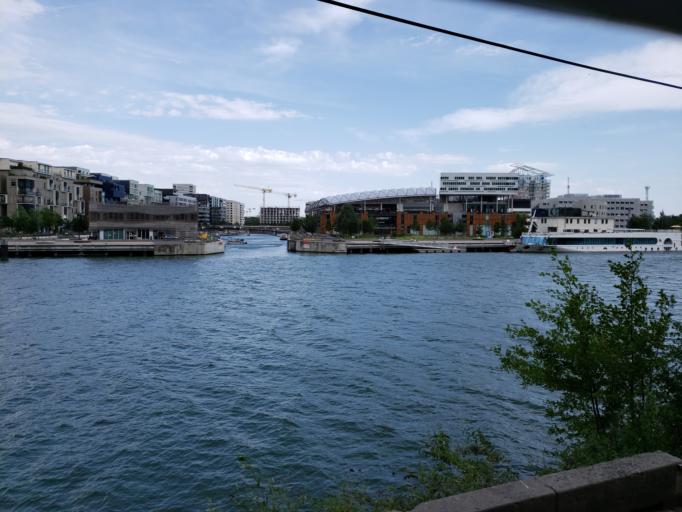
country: FR
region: Rhone-Alpes
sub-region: Departement du Rhone
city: Sainte-Foy-les-Lyon
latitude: 45.7433
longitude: 4.8127
